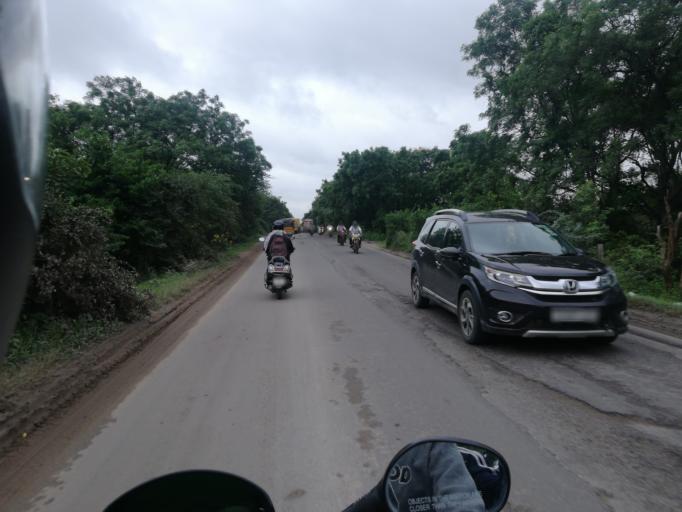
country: IN
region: Telangana
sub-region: Rangareddi
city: Quthbullapur
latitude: 17.5607
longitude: 78.4121
